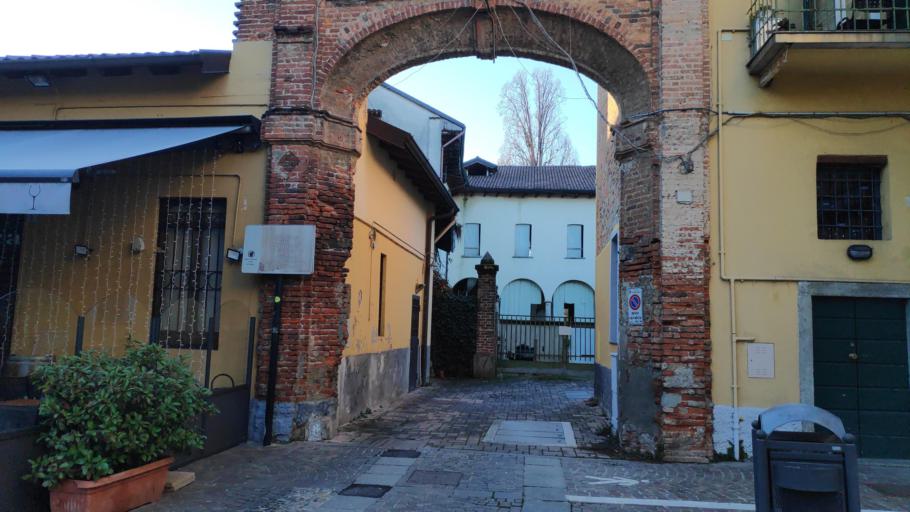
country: IT
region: Lombardy
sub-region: Citta metropolitana di Milano
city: Cologno Monzese
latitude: 45.5304
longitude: 9.2762
